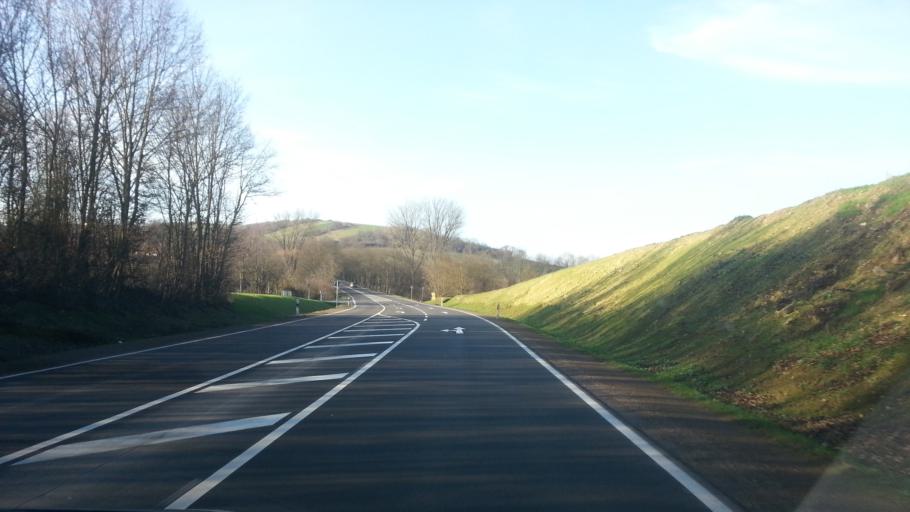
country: DE
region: Rheinland-Pfalz
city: Albisheim
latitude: 49.6512
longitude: 8.1024
